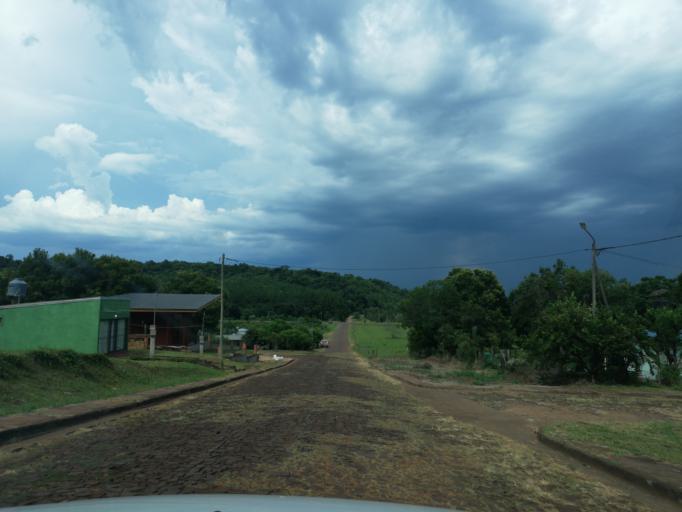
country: AR
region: Misiones
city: Cerro Azul
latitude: -27.5728
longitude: -55.5006
